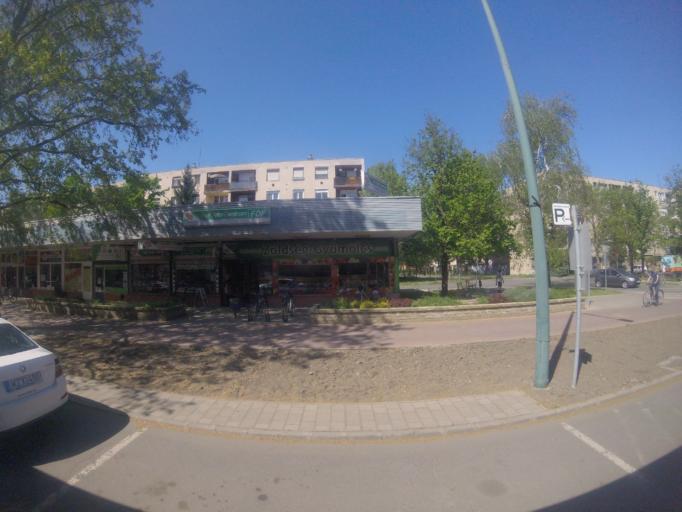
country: HU
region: Bekes
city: Gyula
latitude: 46.6465
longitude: 21.2721
